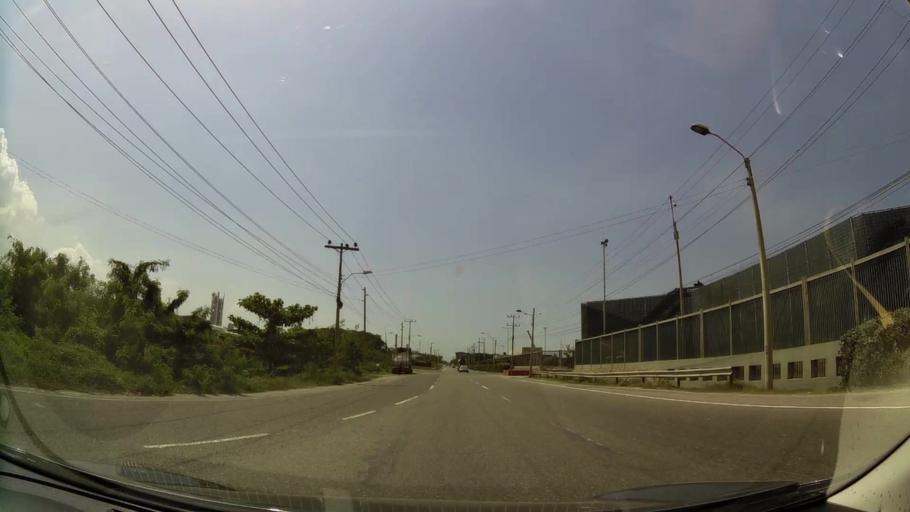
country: CO
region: Bolivar
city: Cartagena
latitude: 10.3442
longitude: -75.4962
